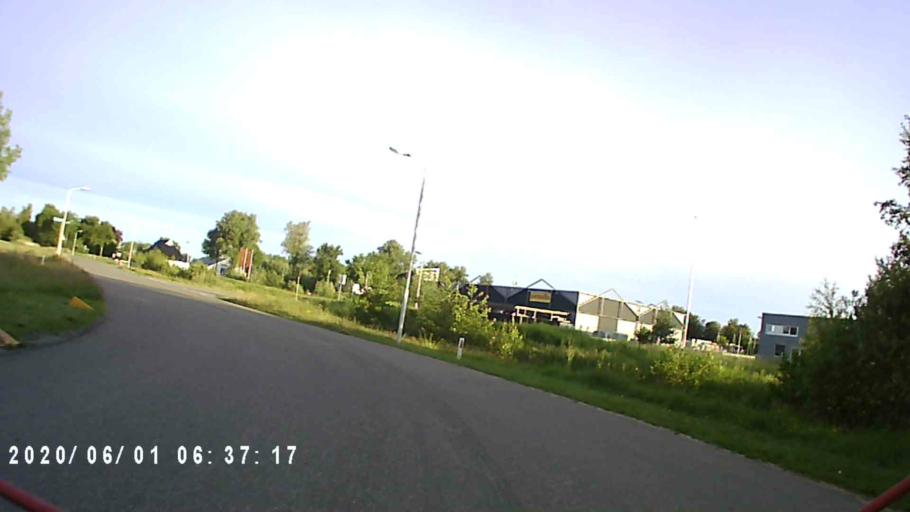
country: NL
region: Friesland
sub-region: Gemeente Kollumerland en Nieuwkruisland
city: Kollum
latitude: 53.2843
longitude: 6.1608
